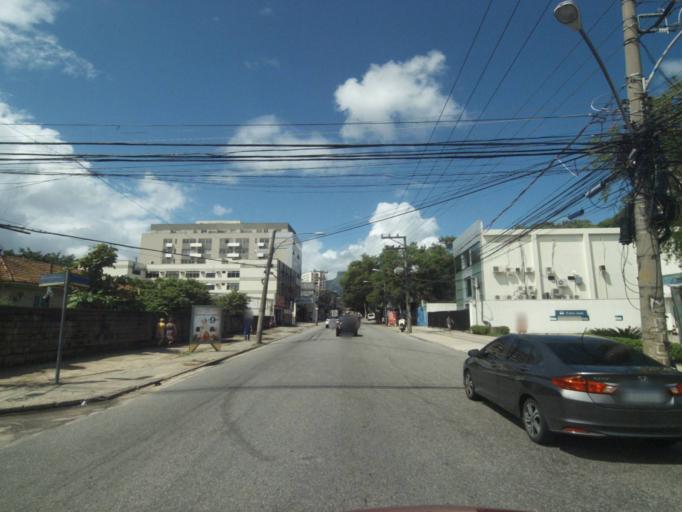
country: BR
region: Rio de Janeiro
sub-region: Sao Joao De Meriti
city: Sao Joao de Meriti
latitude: -22.9276
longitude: -43.3591
